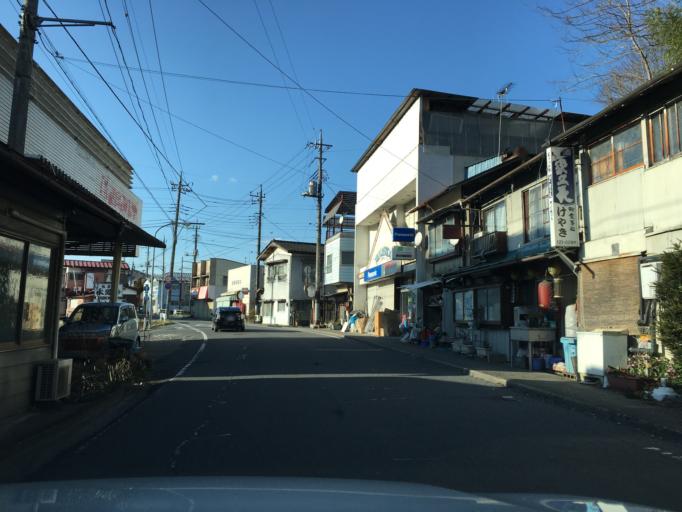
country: JP
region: Ibaraki
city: Daigo
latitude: 36.7733
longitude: 140.3504
